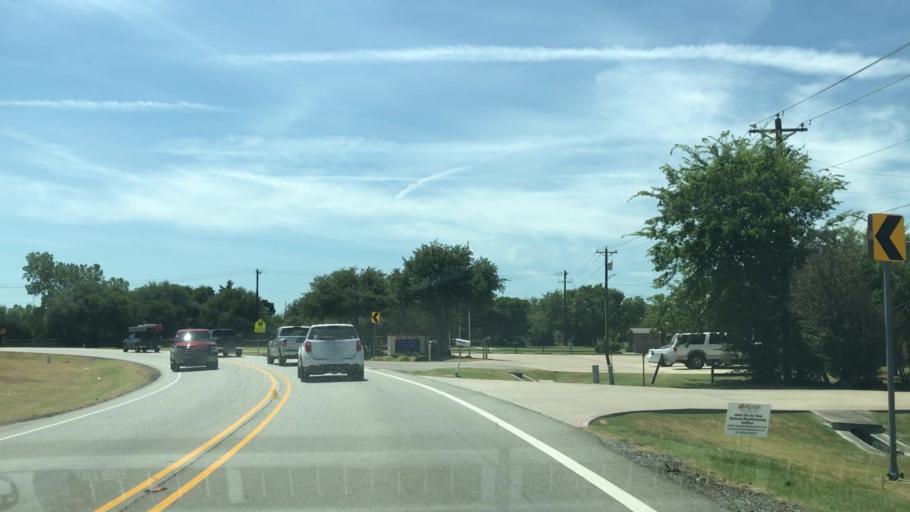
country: US
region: Texas
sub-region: Collin County
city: Lucas
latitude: 33.0933
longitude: -96.5942
